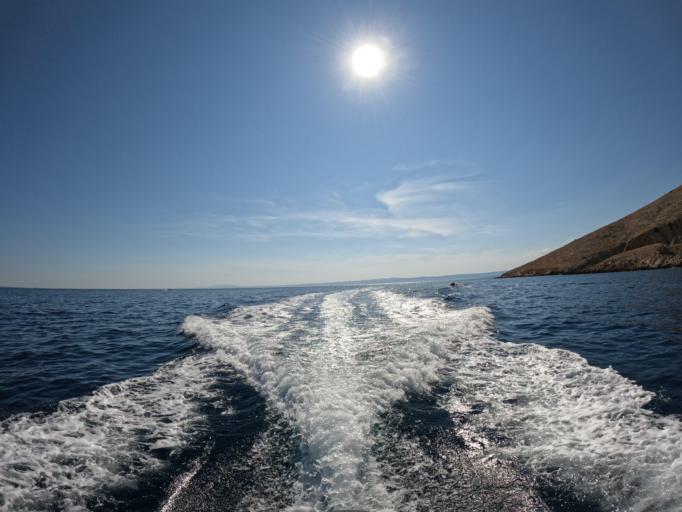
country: HR
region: Primorsko-Goranska
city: Punat
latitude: 44.9639
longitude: 14.6593
